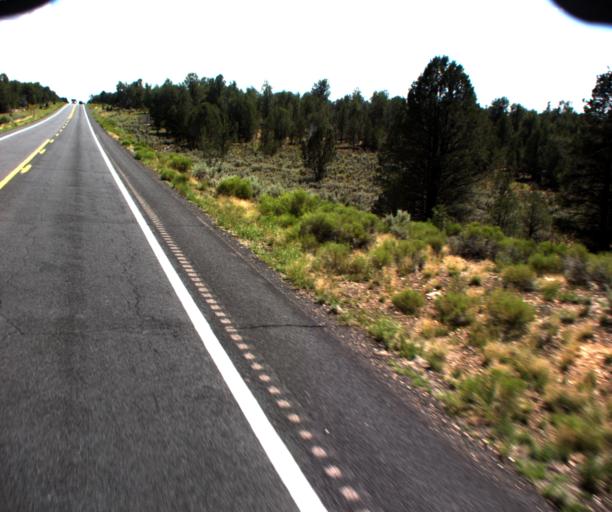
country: US
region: Arizona
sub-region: Coconino County
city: Grand Canyon Village
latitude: 35.8653
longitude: -112.1331
